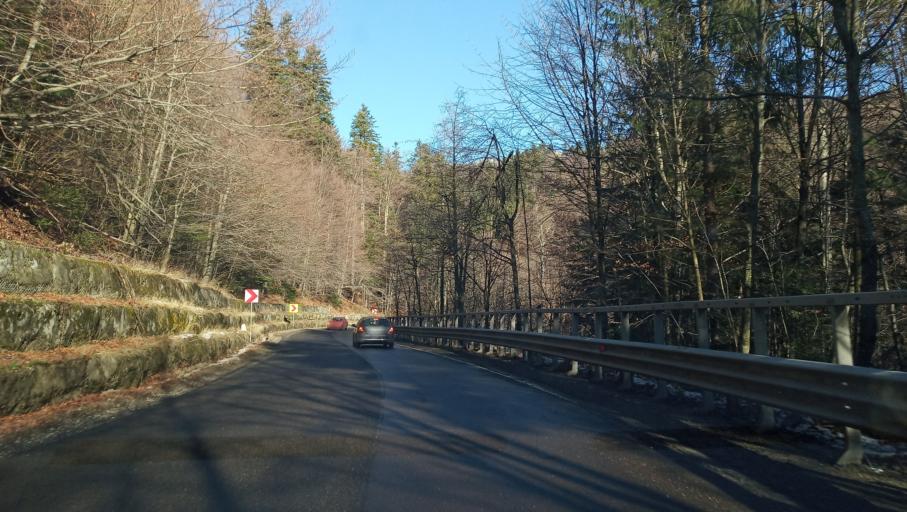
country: RO
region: Brasov
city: Crivina
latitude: 45.4723
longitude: 25.9326
